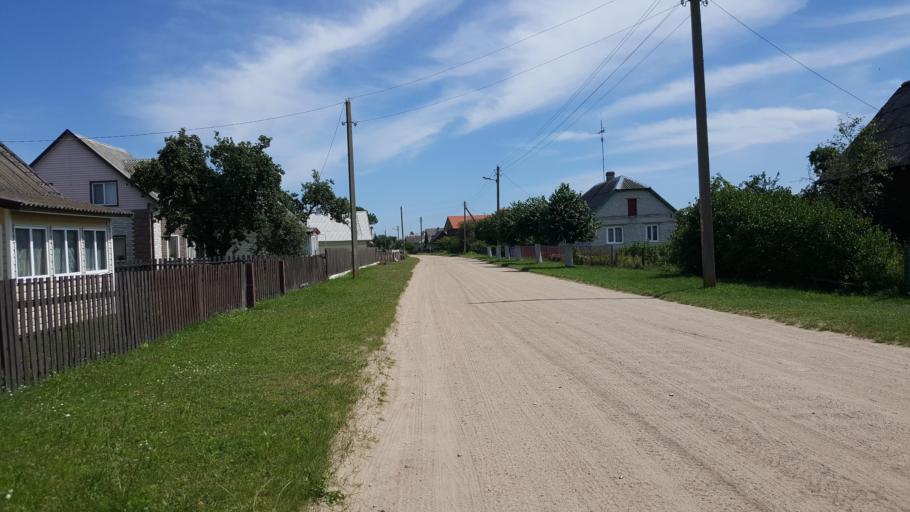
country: BY
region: Brest
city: Pruzhany
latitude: 52.5621
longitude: 24.2079
